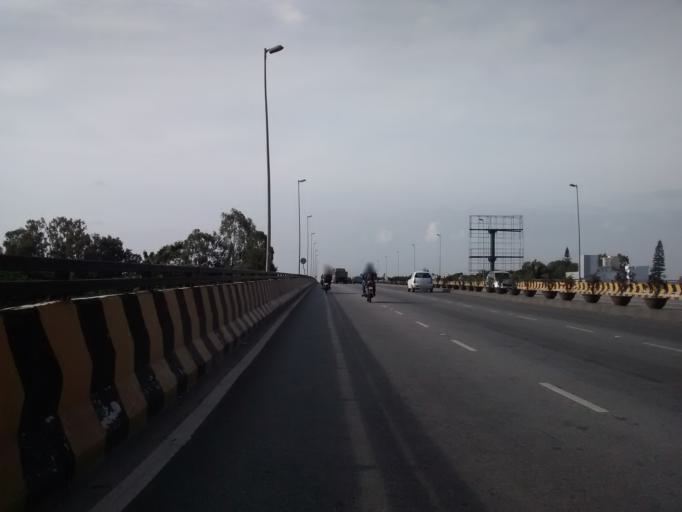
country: IN
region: Karnataka
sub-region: Bangalore Urban
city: Yelahanka
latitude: 13.0706
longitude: 77.5927
